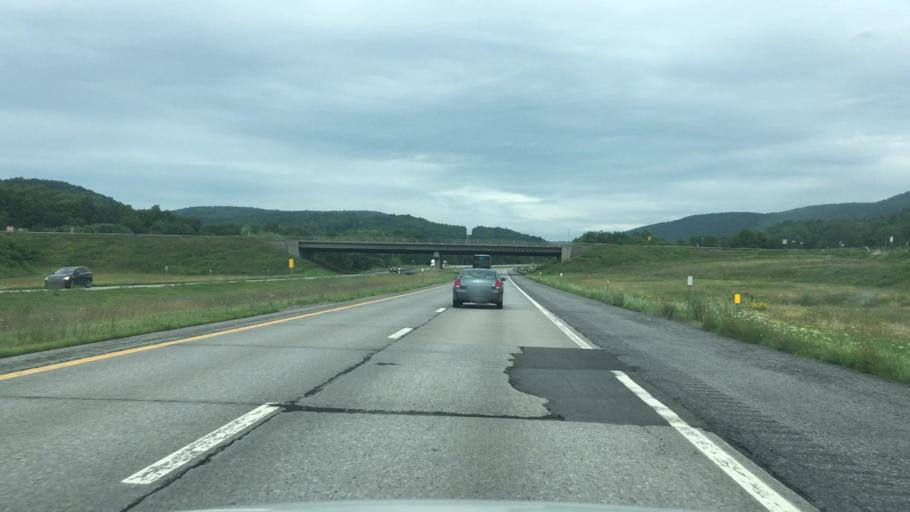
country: US
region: New York
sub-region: Otsego County
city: Worcester
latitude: 42.5910
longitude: -74.7308
